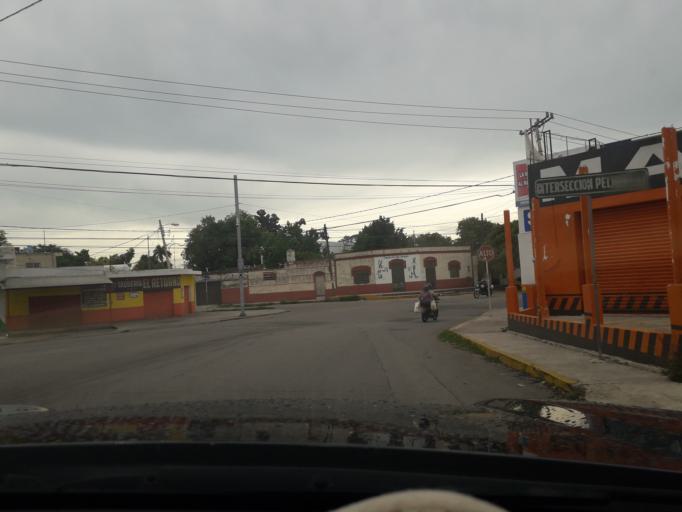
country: MX
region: Yucatan
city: Merida
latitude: 20.9595
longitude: -89.6470
